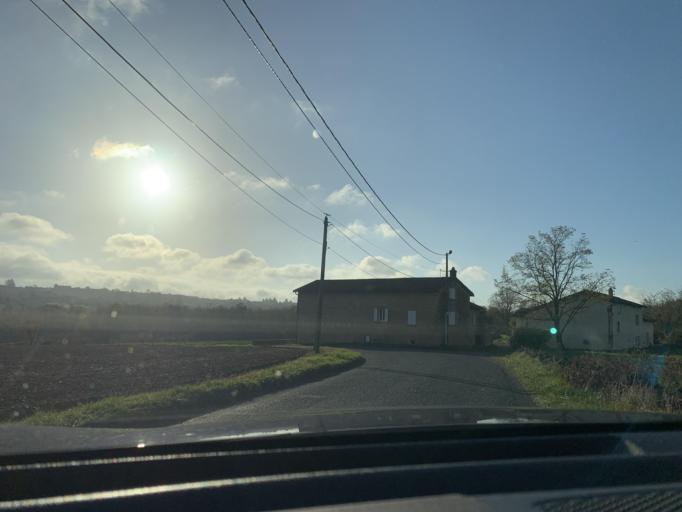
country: FR
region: Rhone-Alpes
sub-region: Departement du Rhone
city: Pommiers
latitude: 45.9478
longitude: 4.6730
